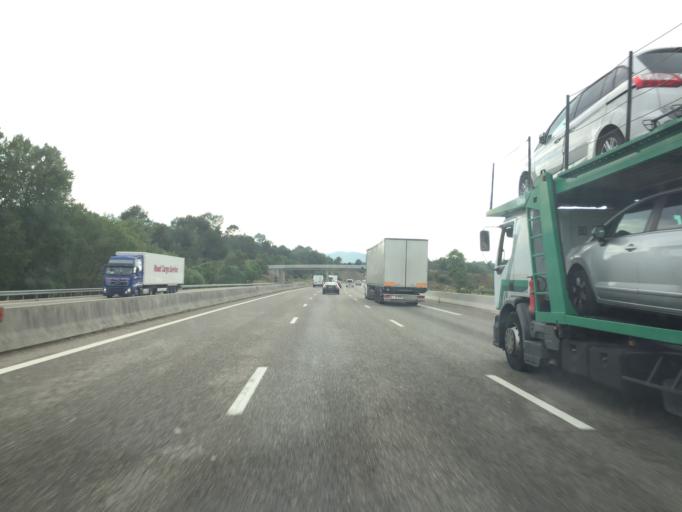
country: FR
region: Provence-Alpes-Cote d'Azur
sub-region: Departement du Var
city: Tourves
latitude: 43.4369
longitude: 5.9146
